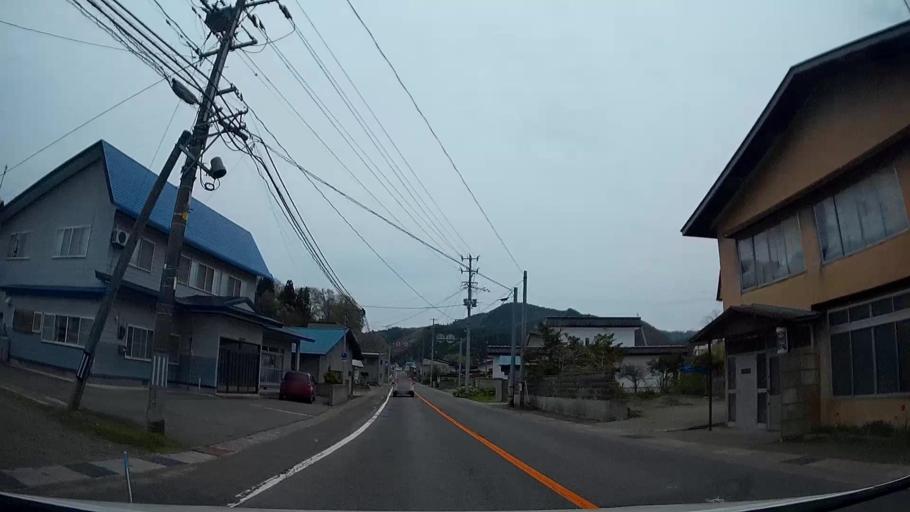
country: JP
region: Akita
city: Hanawa
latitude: 40.2983
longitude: 140.8376
